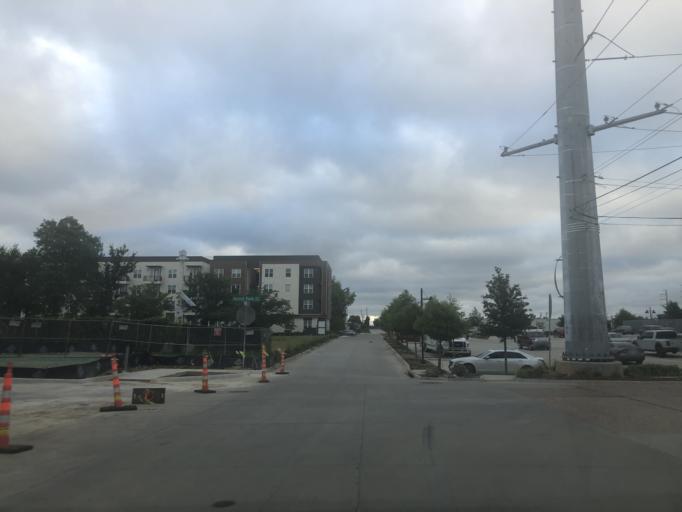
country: US
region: Texas
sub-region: Dallas County
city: University Park
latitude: 32.8267
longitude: -96.8491
